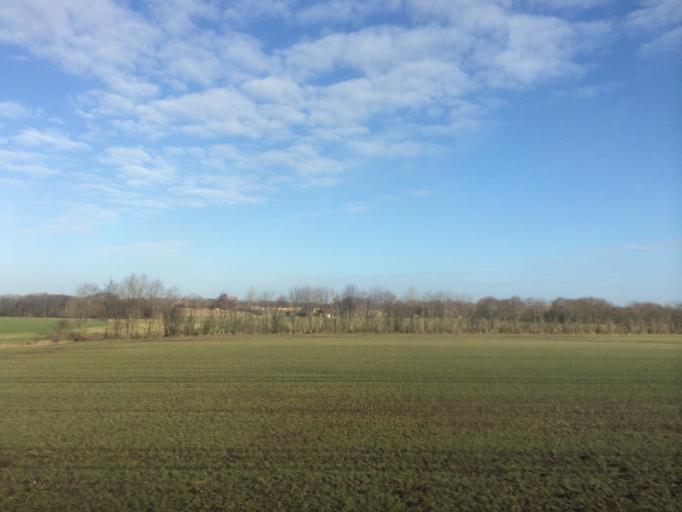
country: DK
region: Central Jutland
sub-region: Herning Kommune
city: Snejbjerg
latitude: 56.1590
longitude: 8.8933
